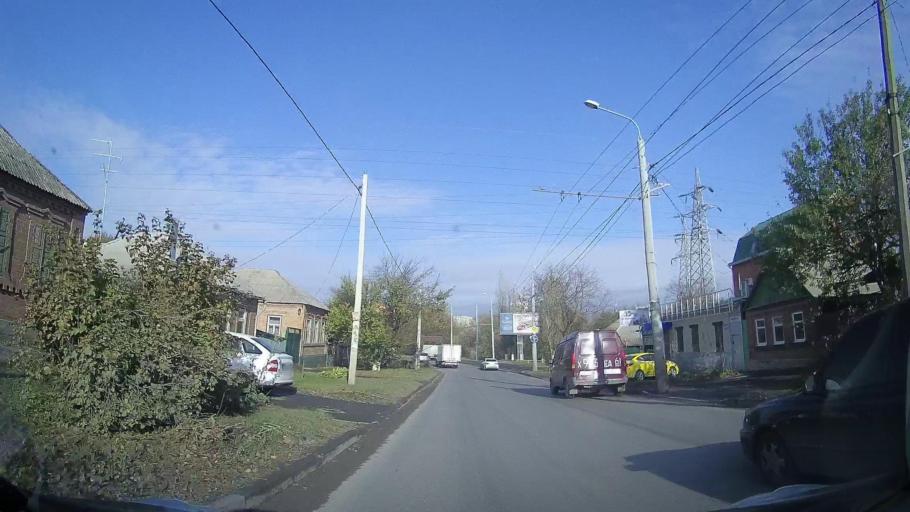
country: RU
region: Rostov
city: Severnyy
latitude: 47.2729
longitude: 39.7200
